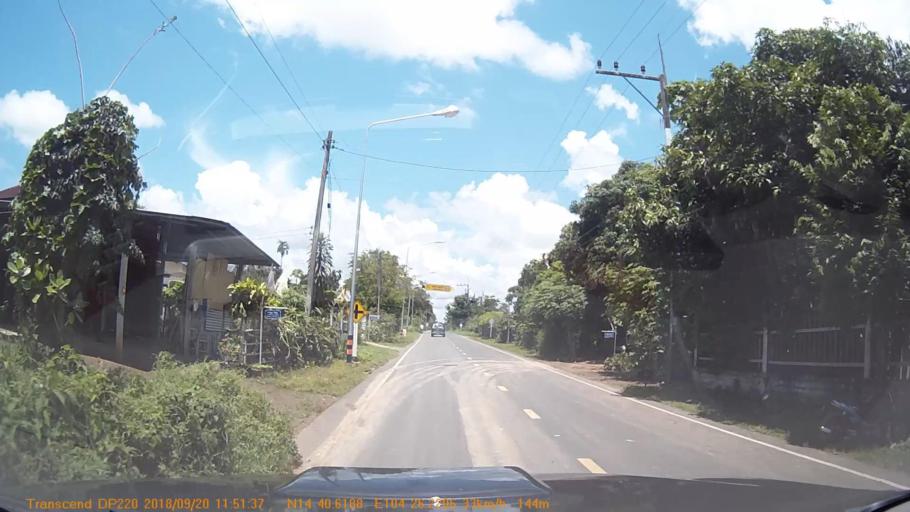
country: TH
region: Sisaket
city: Khun Han
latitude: 14.6772
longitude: 104.4369
